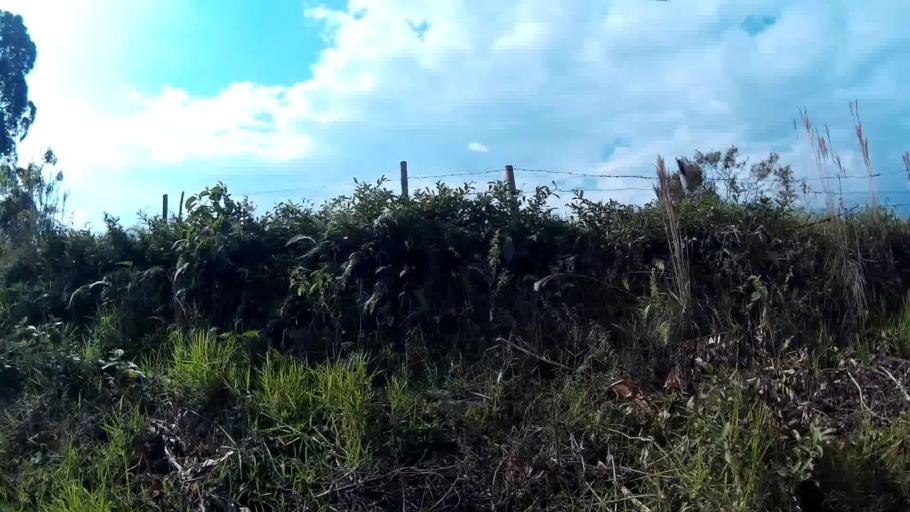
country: CO
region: Quindio
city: Filandia
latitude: 4.6872
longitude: -75.6679
